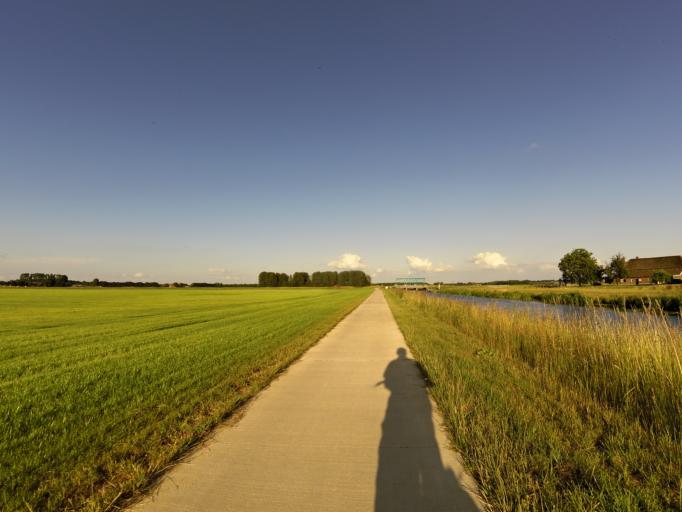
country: NL
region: Gelderland
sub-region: Oude IJsselstreek
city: Gendringen
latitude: 51.8786
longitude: 6.4144
